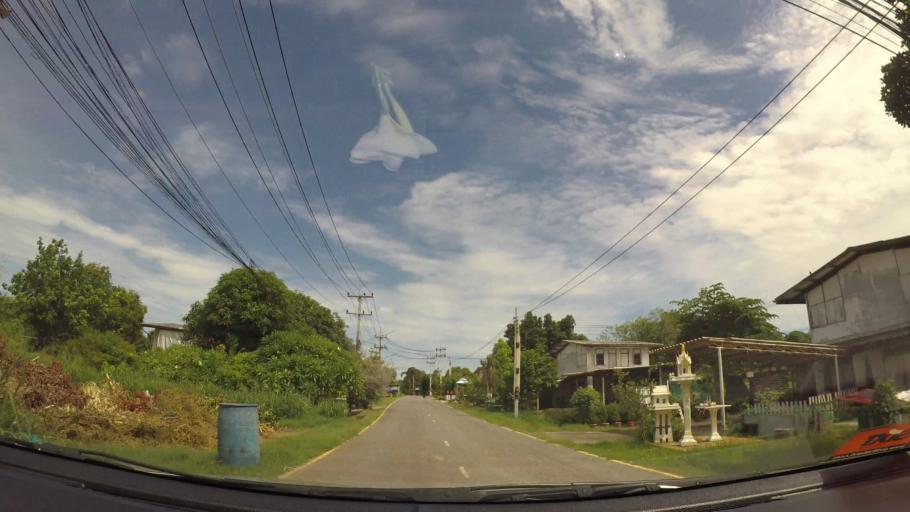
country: TH
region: Chon Buri
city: Sattahip
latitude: 12.6670
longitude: 100.9109
